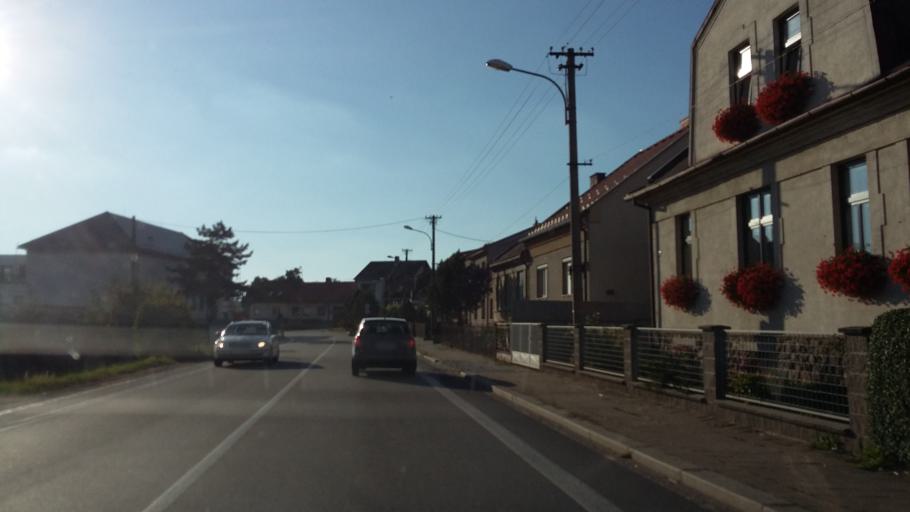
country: CZ
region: Vysocina
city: Merin
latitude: 49.3903
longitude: 15.8923
